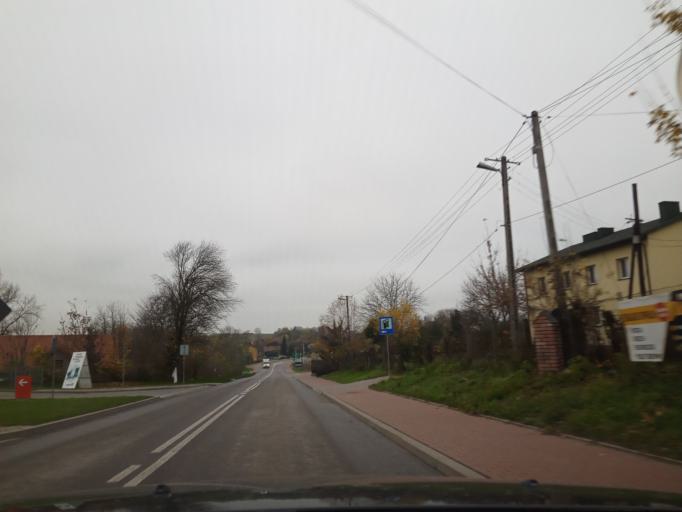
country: PL
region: Swietokrzyskie
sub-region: Powiat pinczowski
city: Dzialoszyce
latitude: 50.3579
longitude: 20.3545
